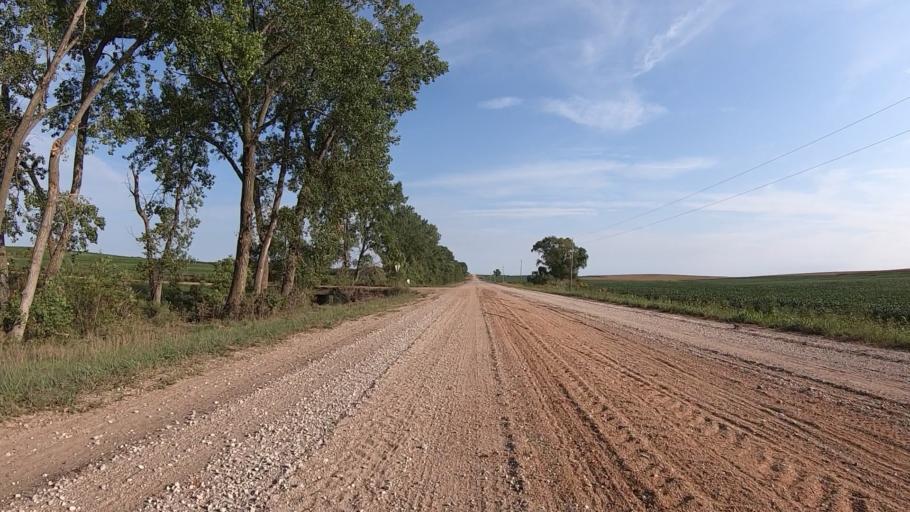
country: US
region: Kansas
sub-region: Marshall County
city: Blue Rapids
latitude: 39.6565
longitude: -96.8629
